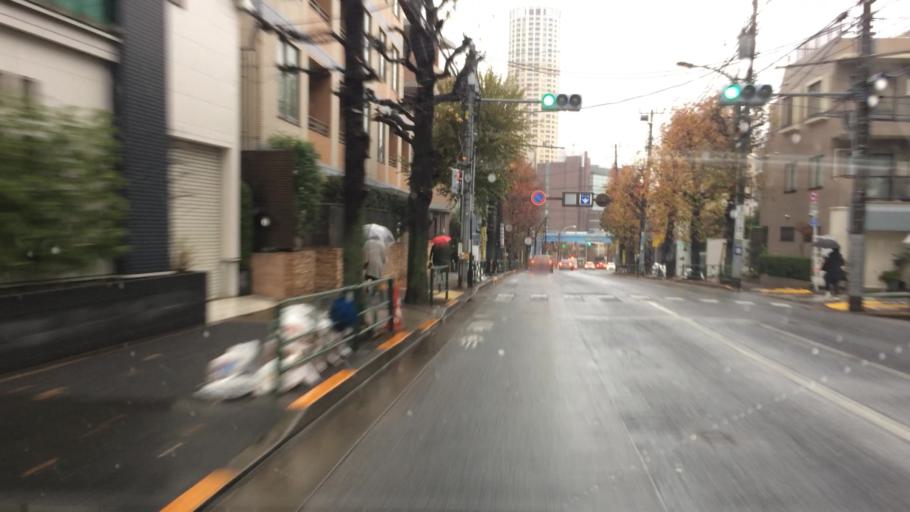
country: JP
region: Tokyo
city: Tokyo
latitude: 35.6386
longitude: 139.6978
